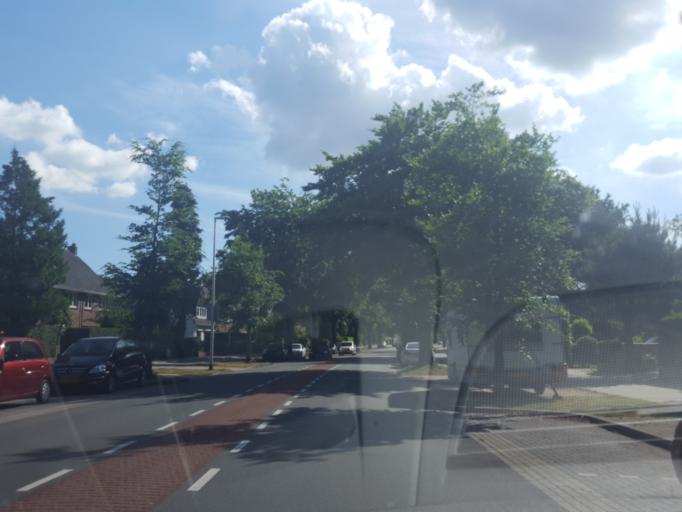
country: NL
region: North Holland
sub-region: Gemeente Bussum
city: Bussum
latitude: 52.2708
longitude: 5.1856
